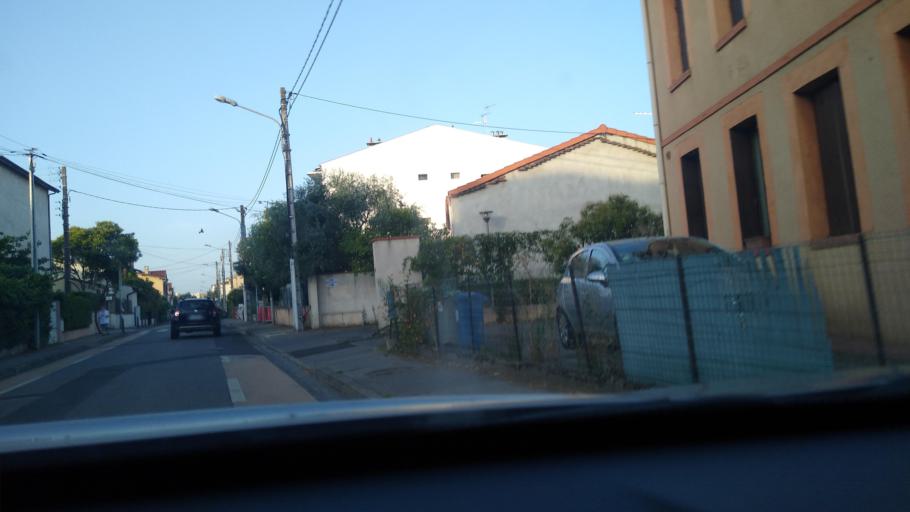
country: FR
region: Midi-Pyrenees
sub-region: Departement de la Haute-Garonne
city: Toulouse
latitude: 43.6285
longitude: 1.4570
